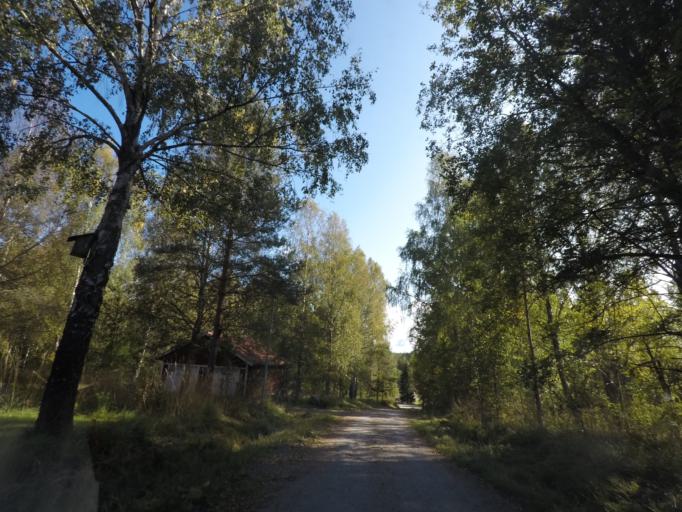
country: SE
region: Vaestmanland
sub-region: Skinnskattebergs Kommun
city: Skinnskatteberg
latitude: 59.8257
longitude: 15.5279
